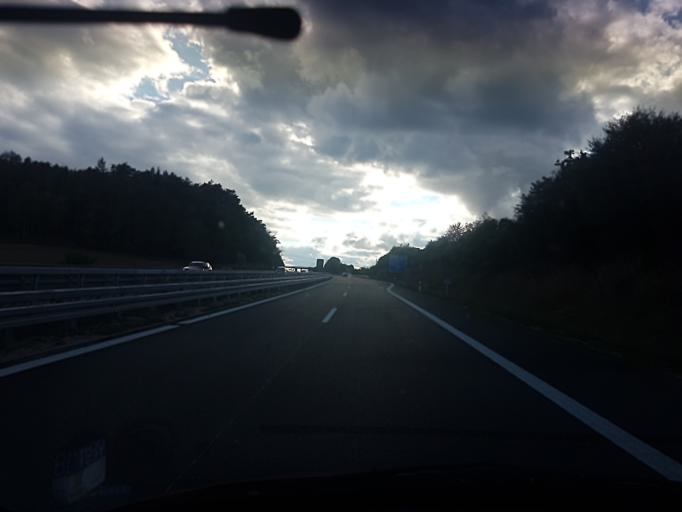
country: DE
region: Bavaria
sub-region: Upper Franconia
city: Wattendorf
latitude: 49.9905
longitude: 11.1277
